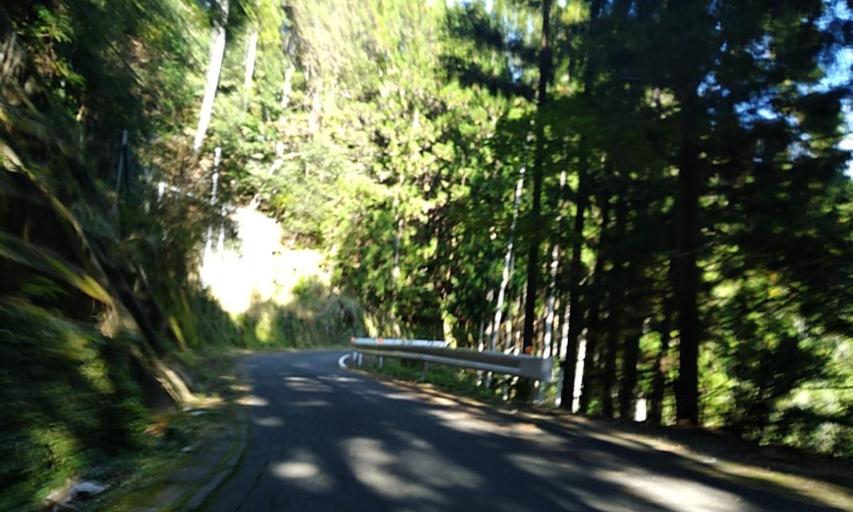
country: JP
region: Wakayama
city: Shingu
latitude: 33.9103
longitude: 135.9880
